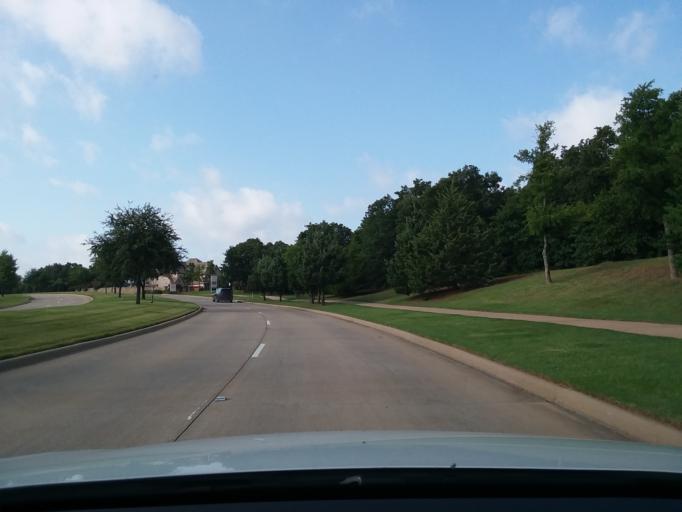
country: US
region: Texas
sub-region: Denton County
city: Copper Canyon
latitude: 33.1038
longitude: -97.1242
